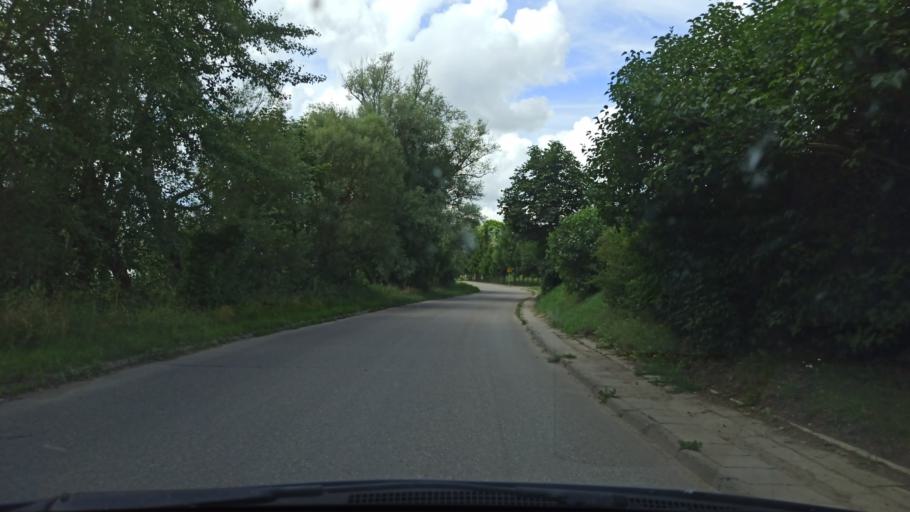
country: PL
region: Warmian-Masurian Voivodeship
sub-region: Powiat ostrodzki
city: Morag
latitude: 53.8636
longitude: 20.0218
